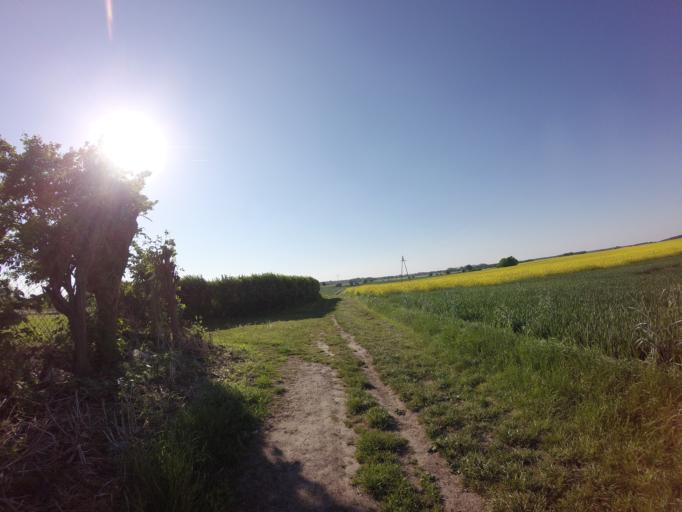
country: PL
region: West Pomeranian Voivodeship
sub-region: Powiat choszczenski
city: Choszczno
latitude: 53.1342
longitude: 15.3738
